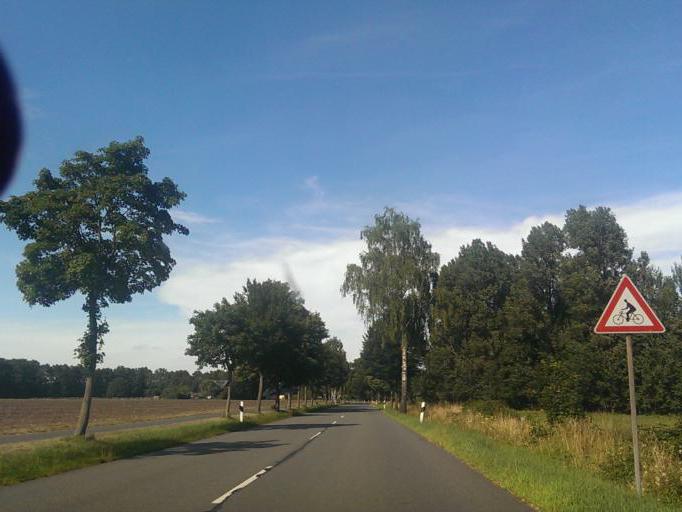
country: DE
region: North Rhine-Westphalia
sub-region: Regierungsbezirk Detmold
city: Hovelhof
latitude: 51.7996
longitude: 8.6676
